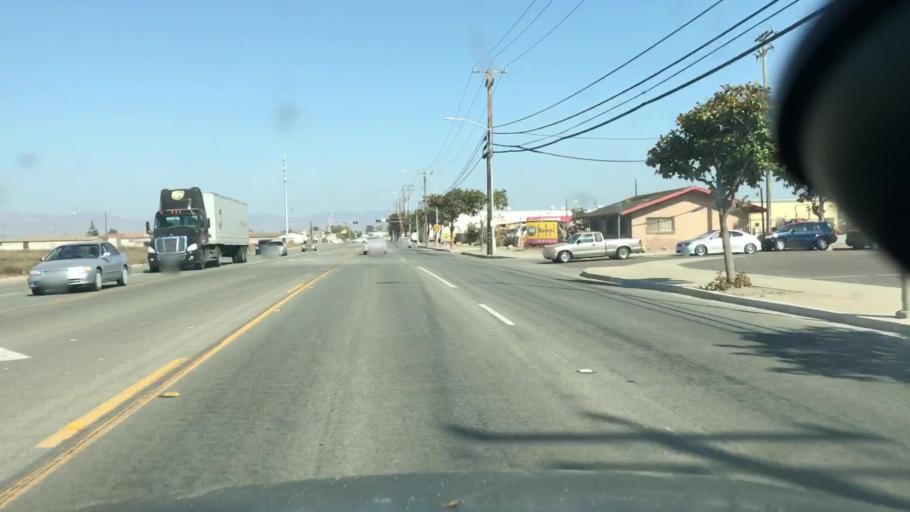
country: US
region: California
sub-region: Santa Barbara County
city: Santa Maria
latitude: 34.9205
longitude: -120.4480
